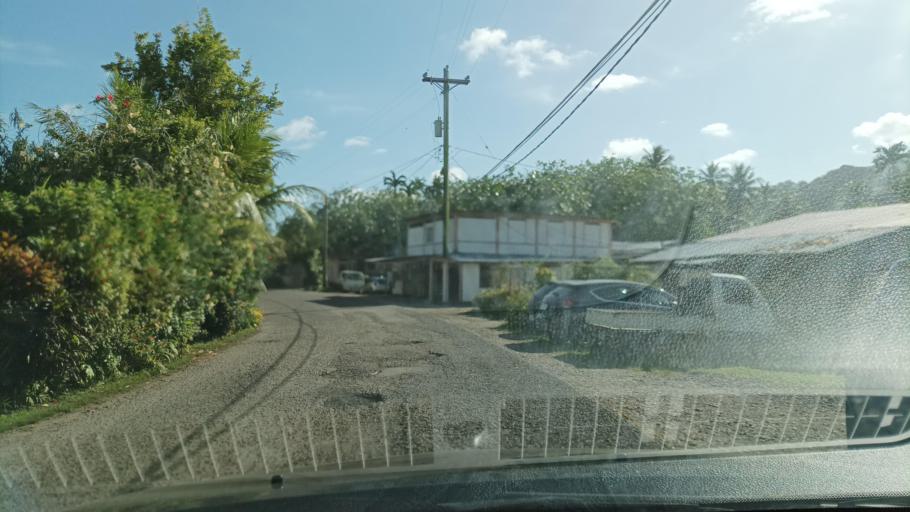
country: FM
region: Kosrae
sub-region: Malem Municipality
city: Malem
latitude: 5.2884
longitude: 163.0266
